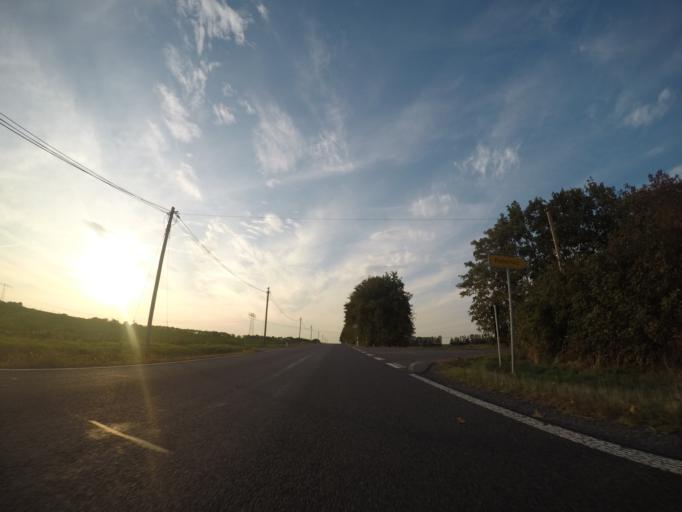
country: DE
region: Thuringia
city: Drogen
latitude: 50.9244
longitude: 12.3326
